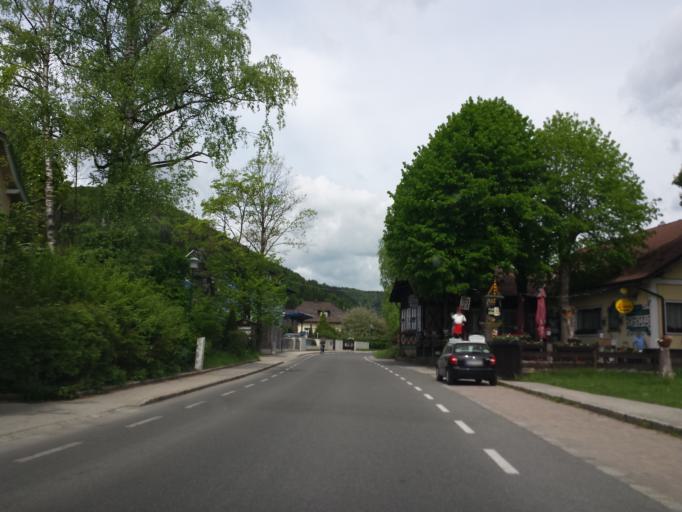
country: AT
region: Lower Austria
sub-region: Politischer Bezirk Wiener Neustadt
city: Pernitz
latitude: 47.9022
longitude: 15.9521
